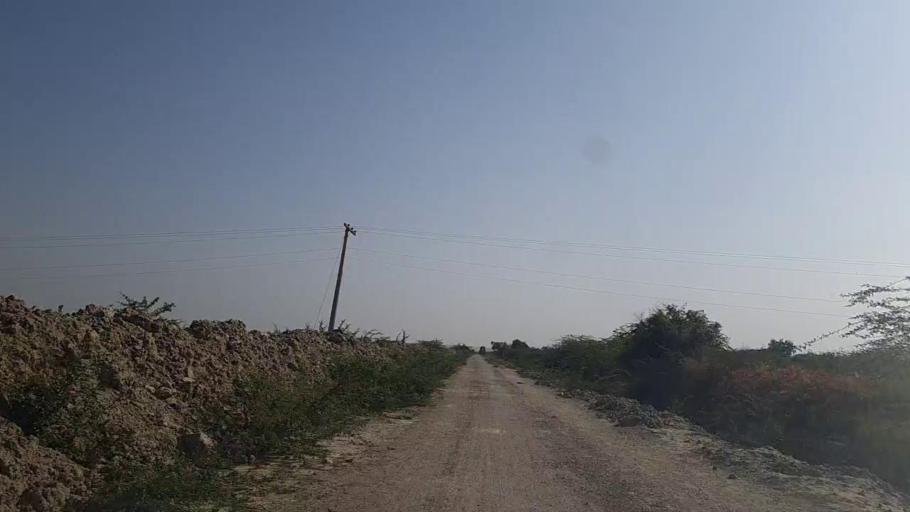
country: PK
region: Sindh
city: Kadhan
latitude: 24.5806
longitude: 69.2628
